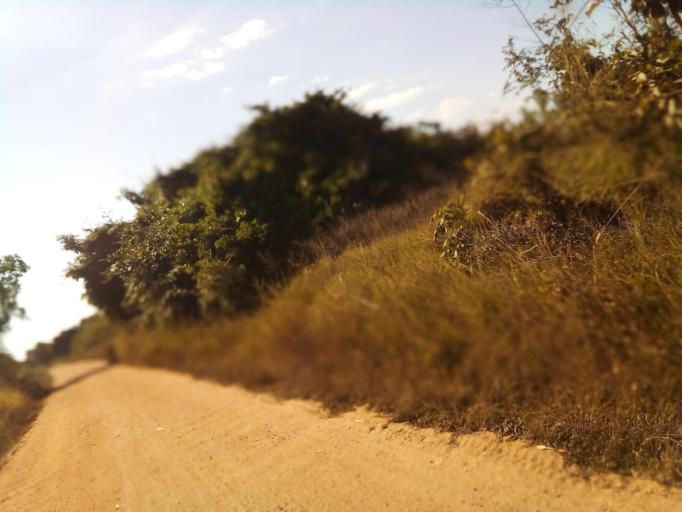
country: MZ
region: Zambezia
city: Quelimane
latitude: -17.5426
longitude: 36.6265
